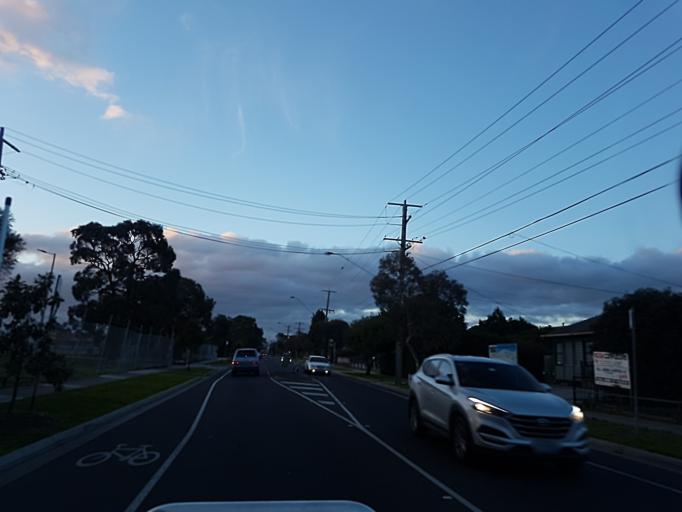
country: AU
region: Victoria
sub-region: Hume
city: Coolaroo
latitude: -37.6699
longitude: 144.9320
